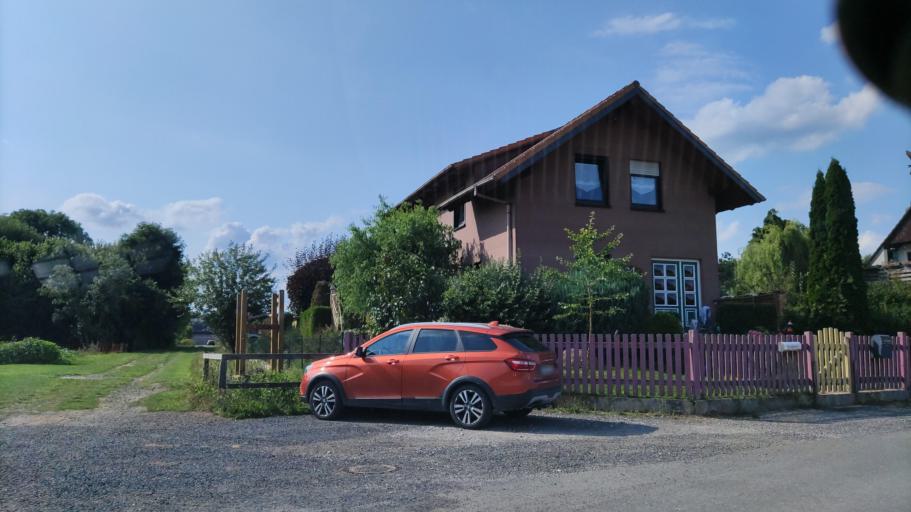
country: DE
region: Lower Saxony
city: Moringen
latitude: 51.7003
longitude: 9.8786
